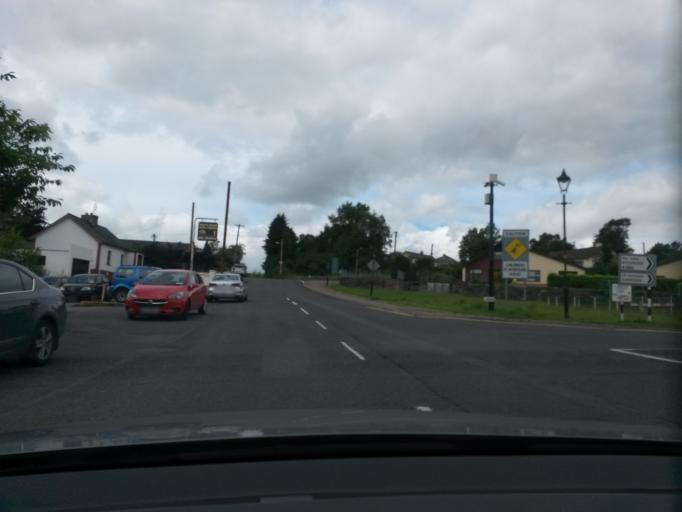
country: IE
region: Connaught
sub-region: County Leitrim
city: Manorhamilton
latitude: 54.3063
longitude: -8.1799
